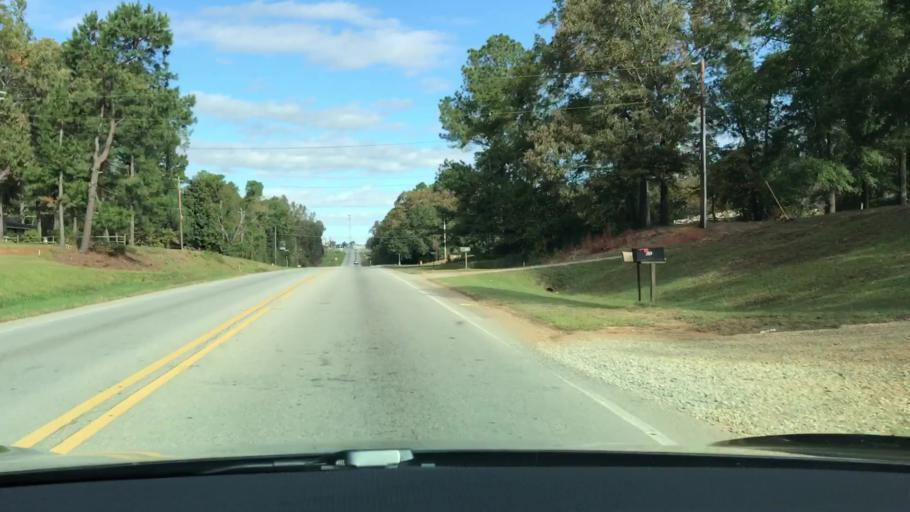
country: US
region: Georgia
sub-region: Jefferson County
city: Louisville
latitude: 32.9981
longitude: -82.3947
